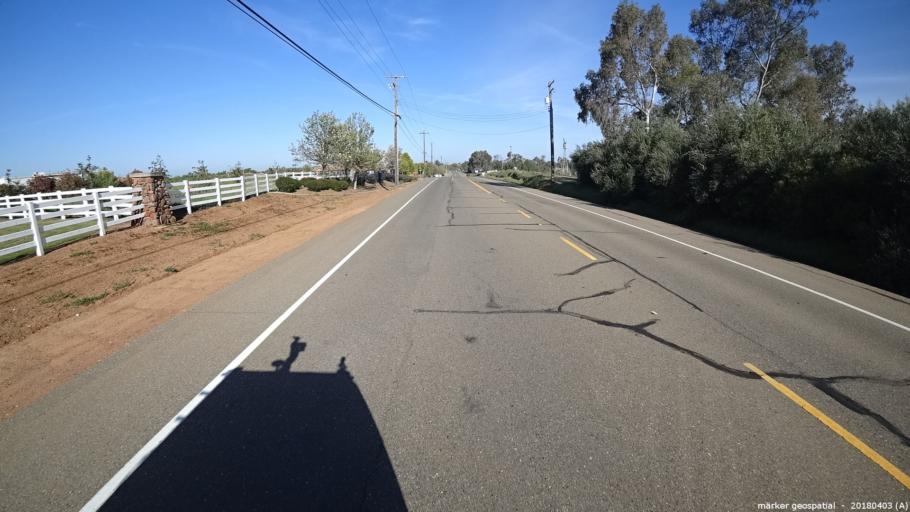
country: US
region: California
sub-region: Sacramento County
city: Wilton
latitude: 38.4232
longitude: -121.1923
